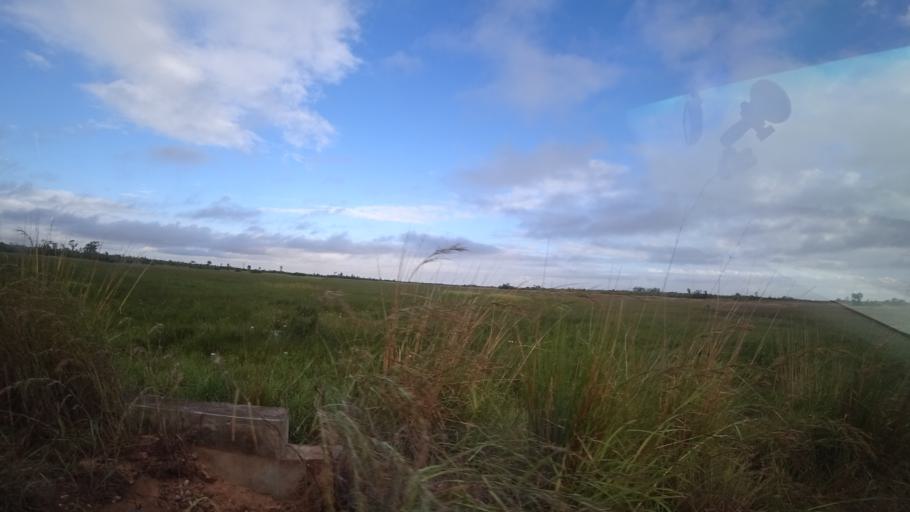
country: MZ
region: Sofala
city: Beira
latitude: -19.6275
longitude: 35.0602
